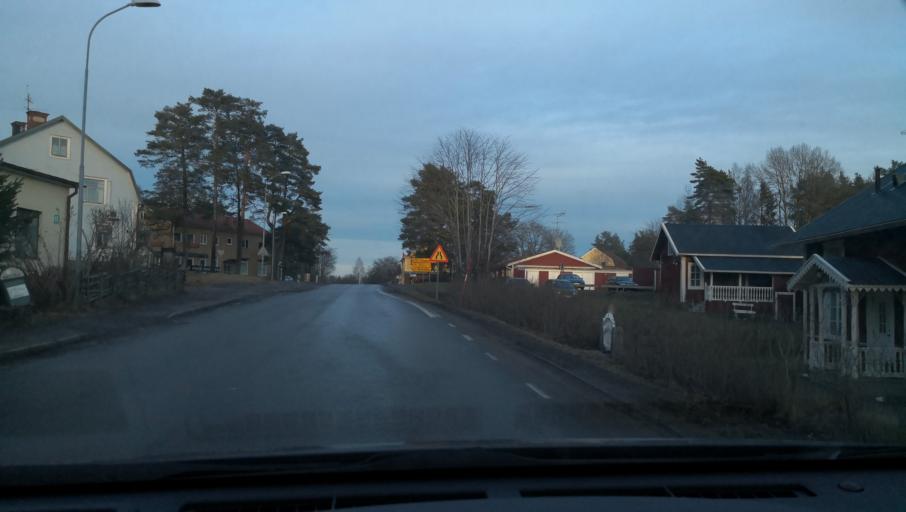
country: SE
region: OErebro
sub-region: Laxa Kommun
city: Laxa
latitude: 59.1517
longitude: 14.6870
